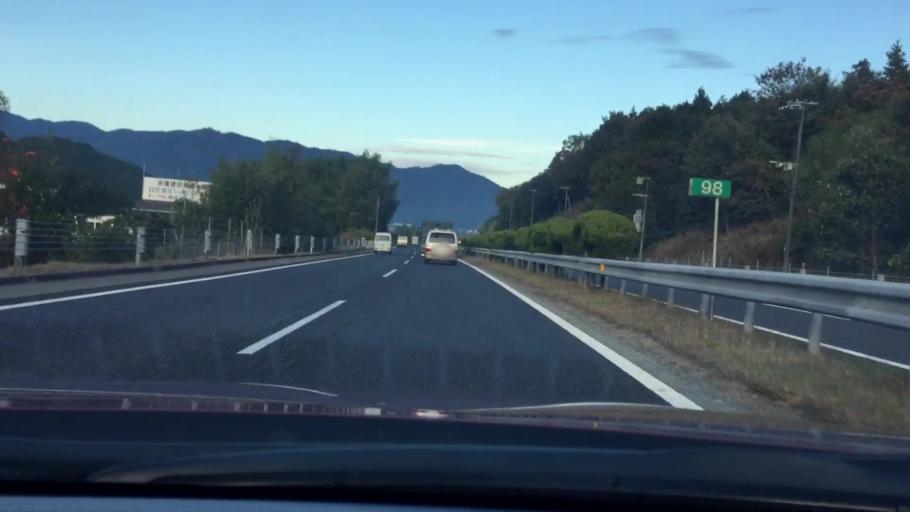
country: JP
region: Hyogo
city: Yamazakicho-nakabirose
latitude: 34.9946
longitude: 134.5690
